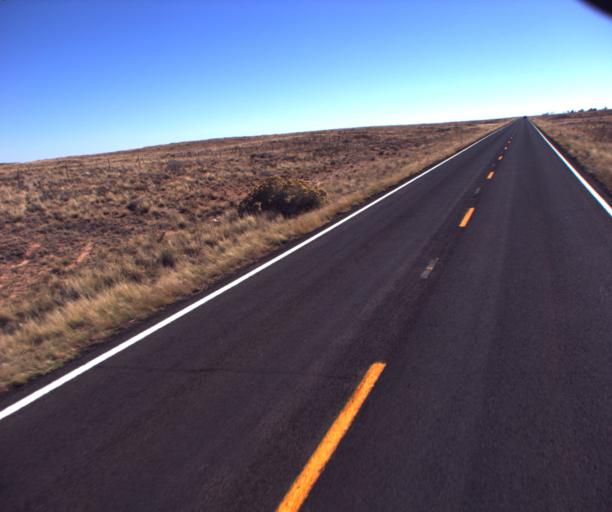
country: US
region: Arizona
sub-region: Coconino County
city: Tuba City
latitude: 35.9678
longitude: -110.9562
